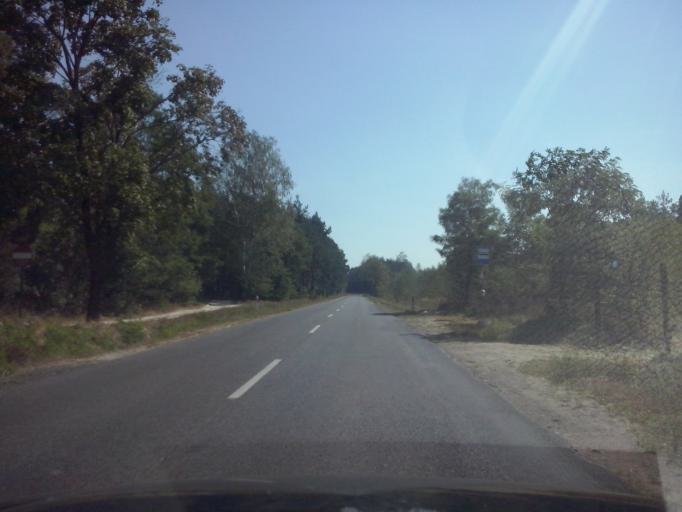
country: PL
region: Swietokrzyskie
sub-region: Powiat kielecki
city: Domaszowice
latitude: 50.8141
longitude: 20.7074
